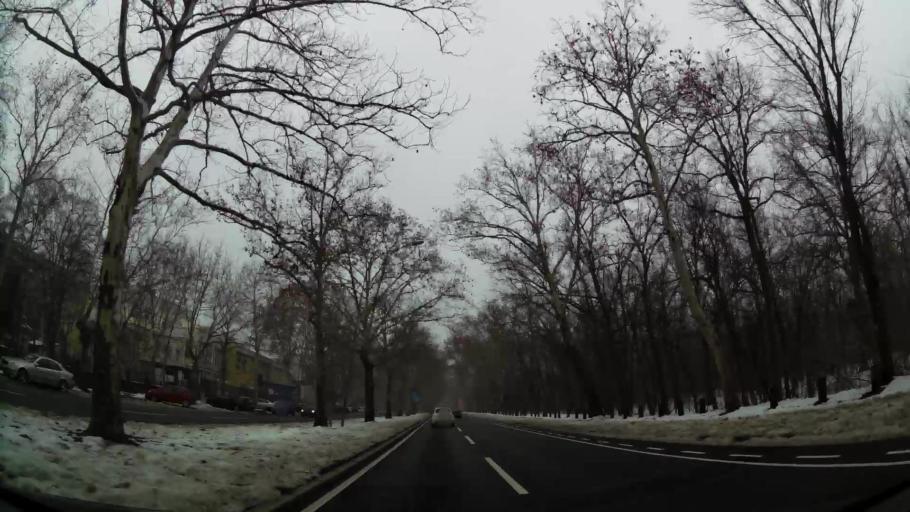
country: RS
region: Central Serbia
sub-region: Belgrade
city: Vozdovac
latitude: 44.7731
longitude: 20.4741
